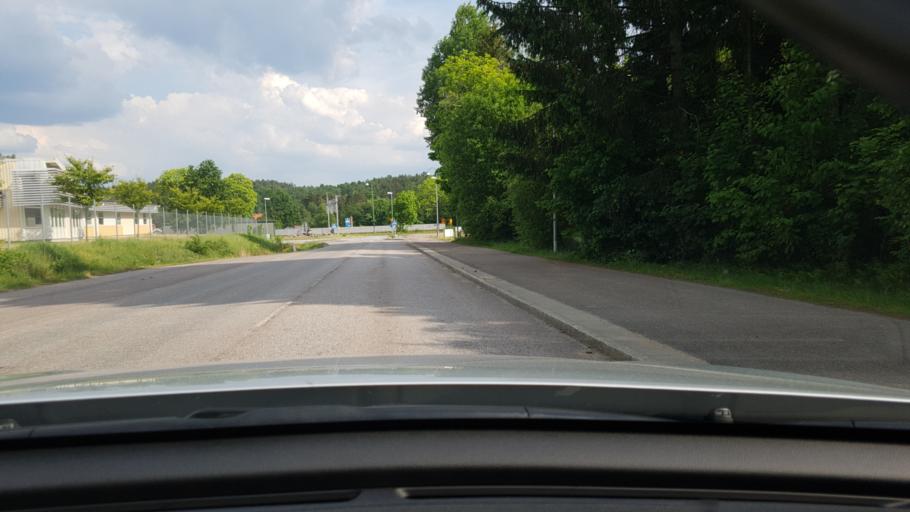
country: SE
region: Vaestra Goetaland
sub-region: Lerums Kommun
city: Stenkullen
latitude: 57.7960
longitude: 12.3163
